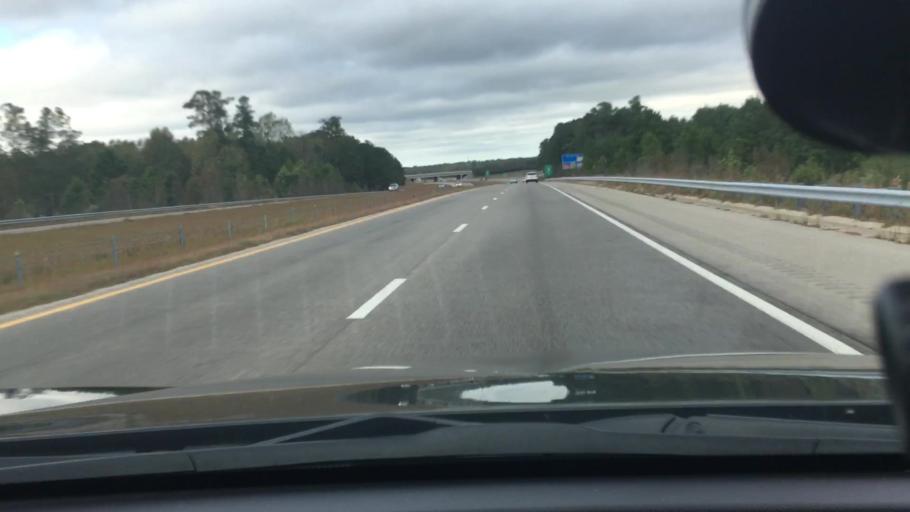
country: US
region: North Carolina
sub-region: Wilson County
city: Lucama
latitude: 35.7545
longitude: -78.0245
